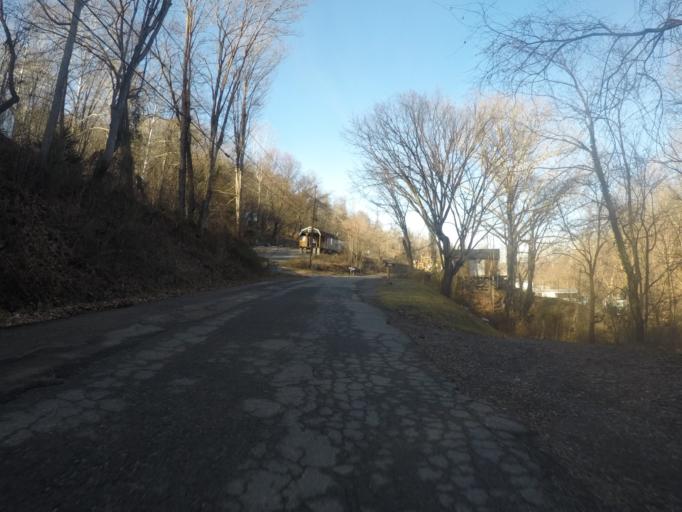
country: US
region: West Virginia
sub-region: Cabell County
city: Huntington
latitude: 38.3955
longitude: -82.4875
